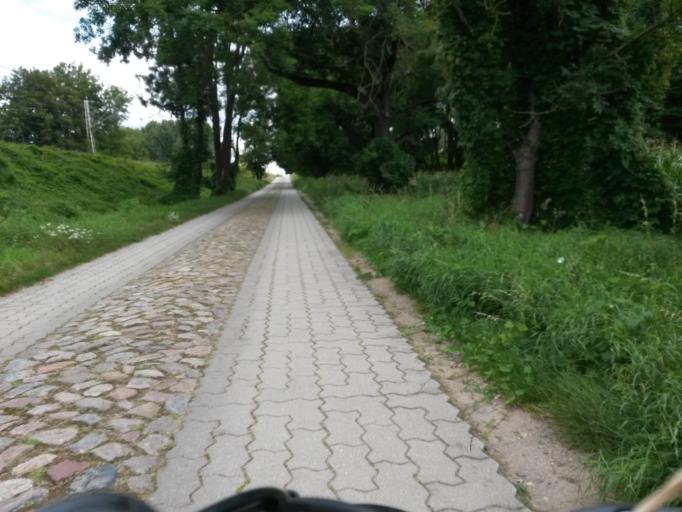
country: DE
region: Brandenburg
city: Pinnow
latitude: 53.1018
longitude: 14.0289
